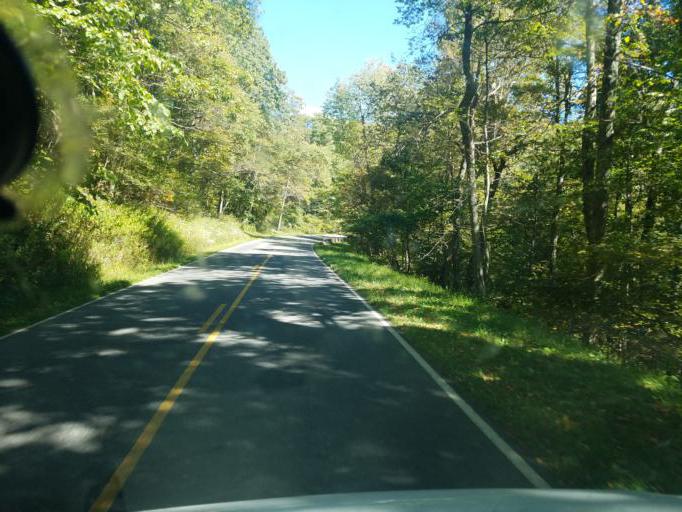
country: US
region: Virginia
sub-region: Rockingham County
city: Elkton
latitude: 38.3882
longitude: -78.5141
